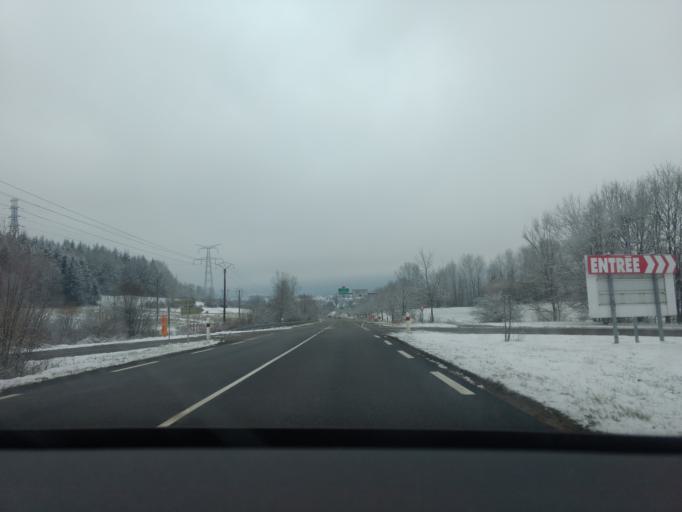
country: FR
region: Franche-Comte
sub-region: Departement du Jura
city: Champagnole
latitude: 46.7663
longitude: 5.9051
